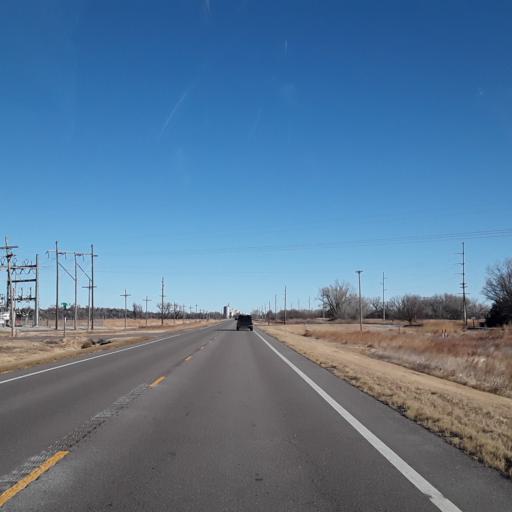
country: US
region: Kansas
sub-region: Pawnee County
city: Larned
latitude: 38.1592
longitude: -99.1226
